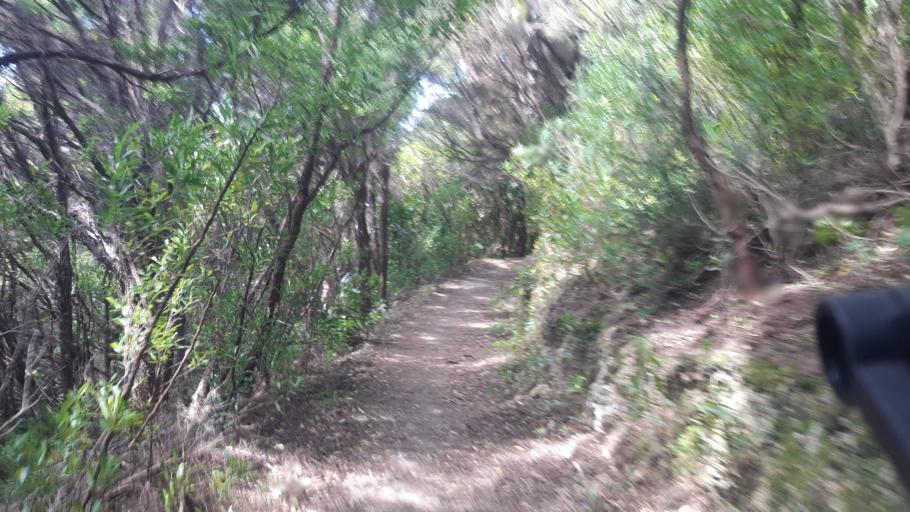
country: NZ
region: Marlborough
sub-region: Marlborough District
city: Picton
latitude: -41.2544
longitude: 174.0427
